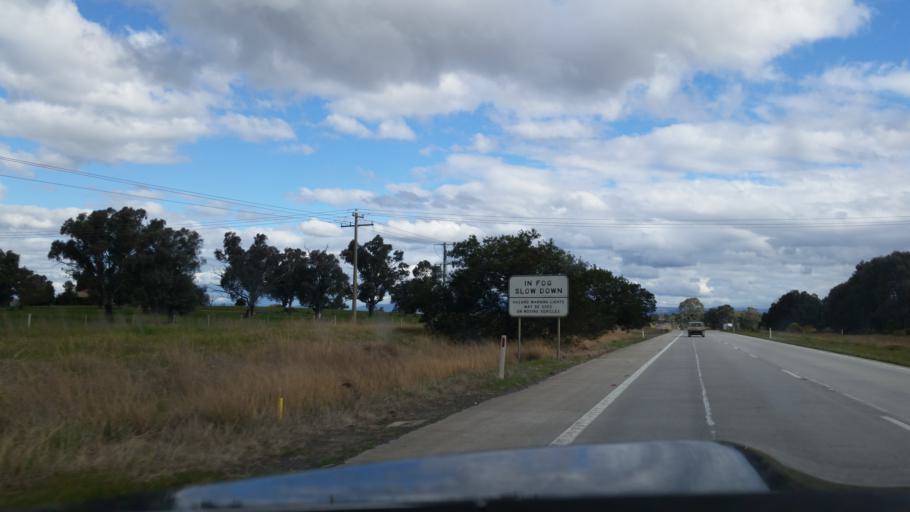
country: AU
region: New South Wales
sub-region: Albury Municipality
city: Lavington
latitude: -35.9913
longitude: 146.9953
